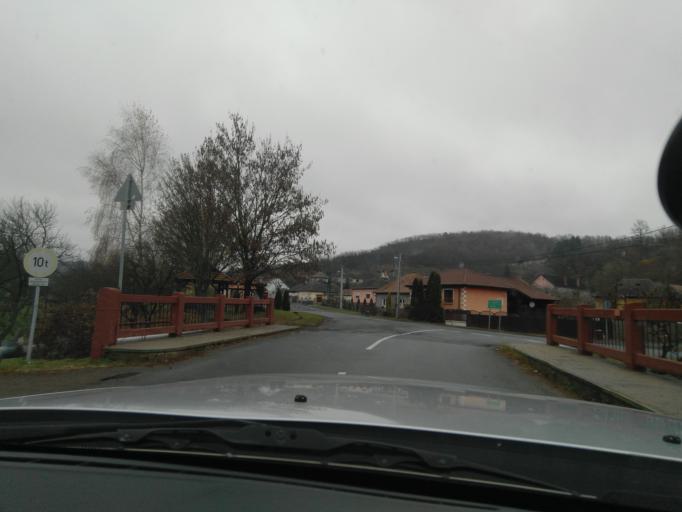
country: HU
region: Nograd
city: Kazar
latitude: 48.0492
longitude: 19.9000
